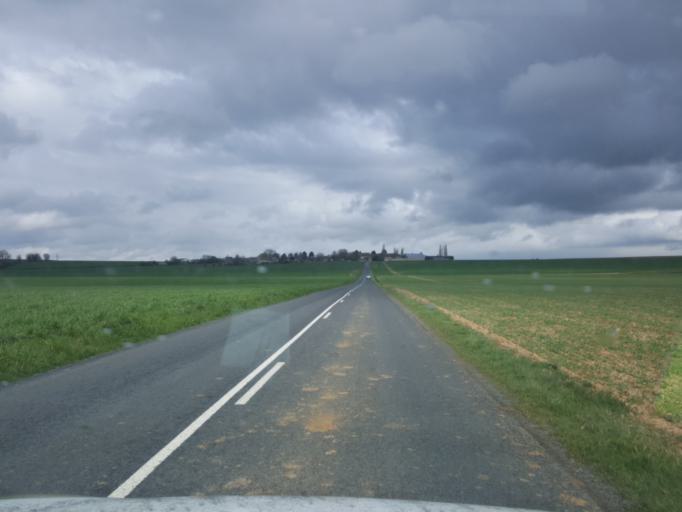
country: FR
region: Ile-de-France
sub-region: Departement du Val-d'Oise
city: Magny-en-Vexin
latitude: 49.2101
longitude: 1.8071
